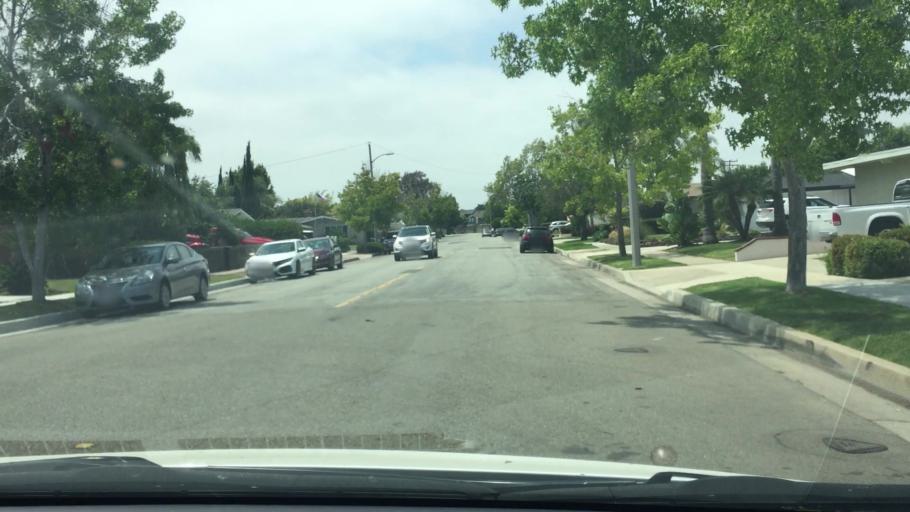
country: US
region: California
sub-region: Orange County
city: Costa Mesa
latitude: 33.6669
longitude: -117.9160
